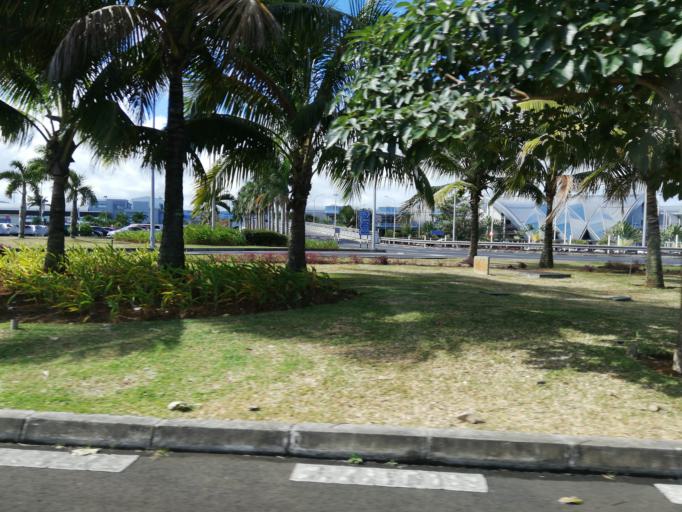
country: MU
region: Grand Port
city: Plaine Magnien
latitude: -20.4343
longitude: 57.6766
